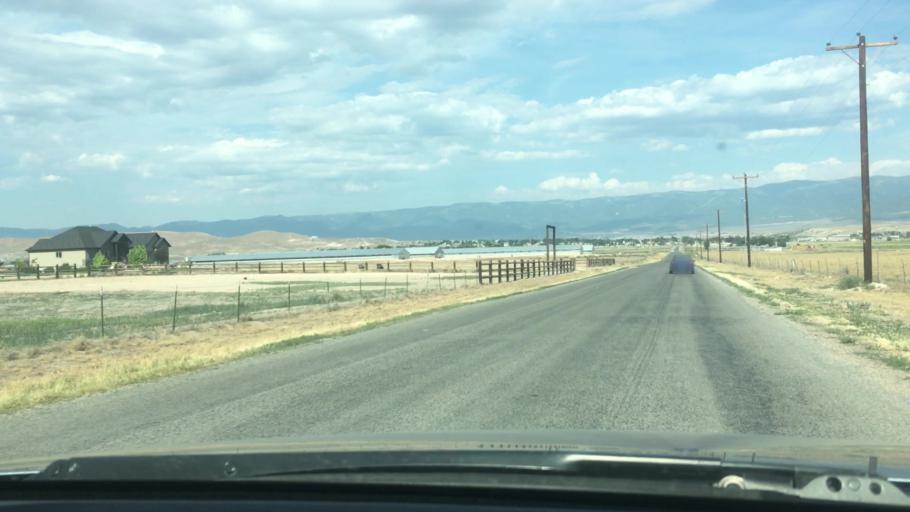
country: US
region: Utah
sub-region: Sanpete County
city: Moroni
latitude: 39.5235
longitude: -111.6251
